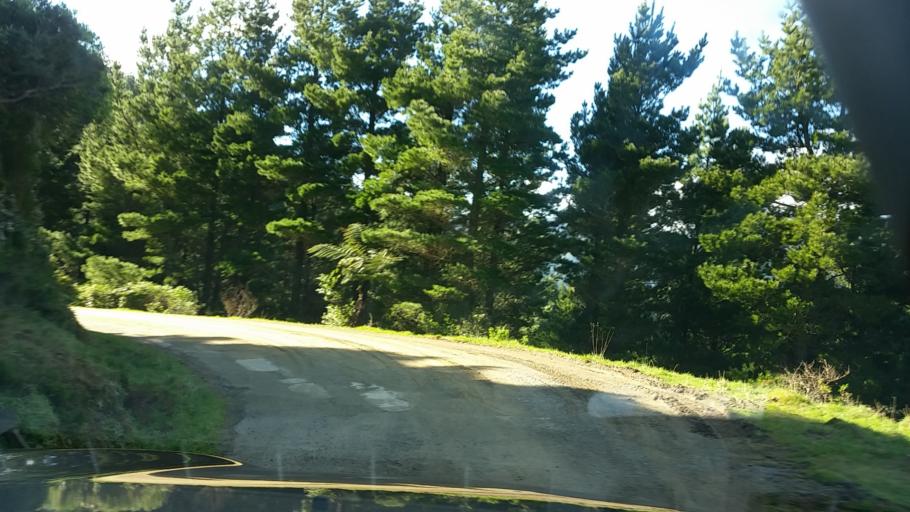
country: NZ
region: Marlborough
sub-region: Marlborough District
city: Picton
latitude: -40.9873
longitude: 173.8141
